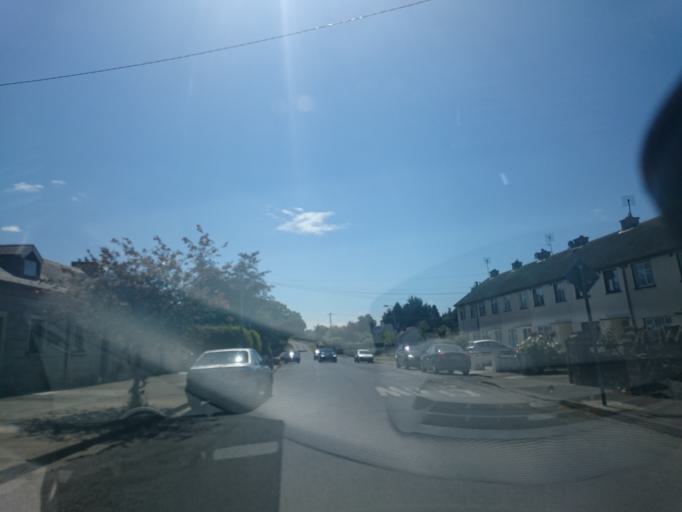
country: IE
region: Leinster
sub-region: County Carlow
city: Bagenalstown
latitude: 52.6292
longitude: -6.9938
